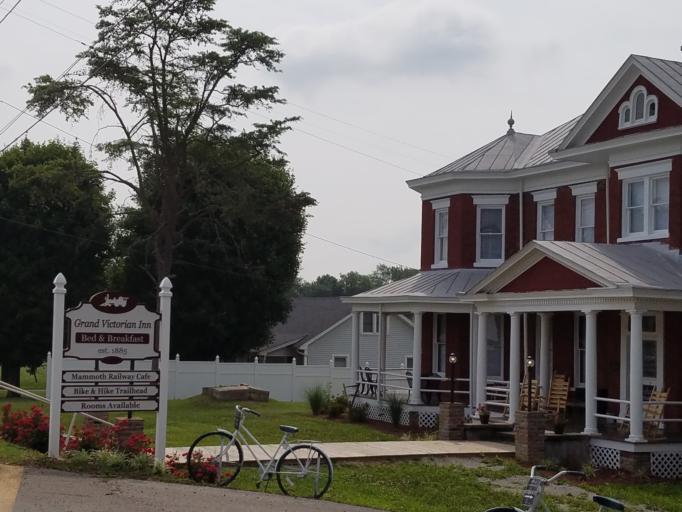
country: US
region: Kentucky
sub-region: Barren County
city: Cave City
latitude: 37.0920
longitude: -86.0482
